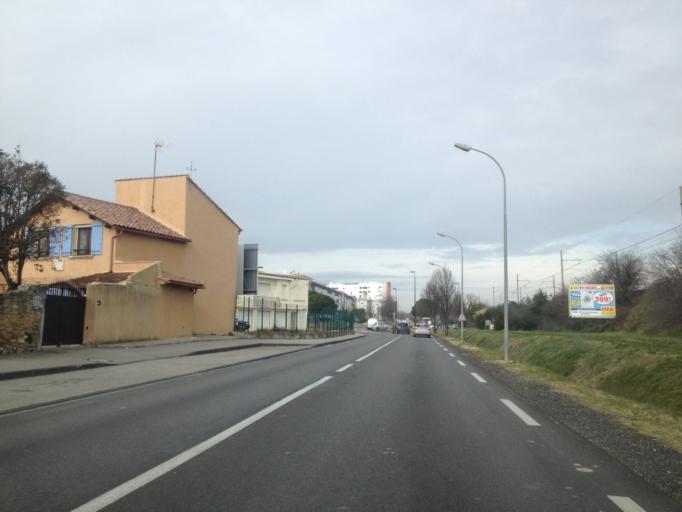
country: FR
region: Provence-Alpes-Cote d'Azur
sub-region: Departement du Vaucluse
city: Orange
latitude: 44.1464
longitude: 4.8101
